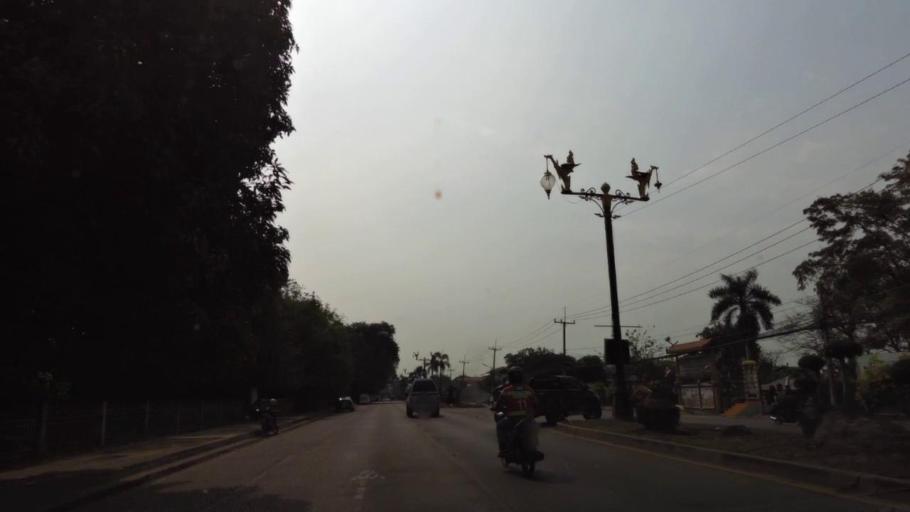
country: TH
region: Phra Nakhon Si Ayutthaya
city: Phra Nakhon Si Ayutthaya
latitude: 14.3502
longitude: 100.5662
